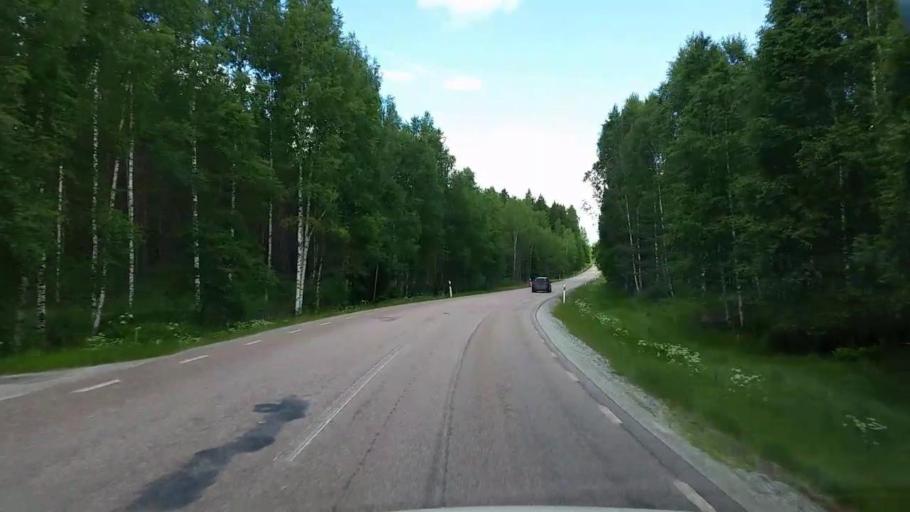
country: SE
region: Vaestmanland
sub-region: Fagersta Kommun
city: Fagersta
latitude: 59.9378
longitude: 15.8123
